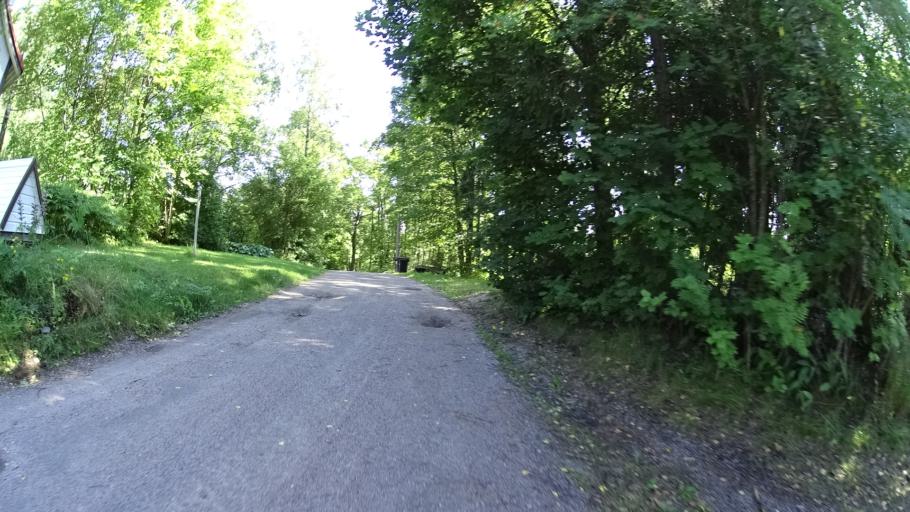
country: FI
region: Uusimaa
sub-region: Helsinki
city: Espoo
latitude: 60.2262
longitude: 24.6811
